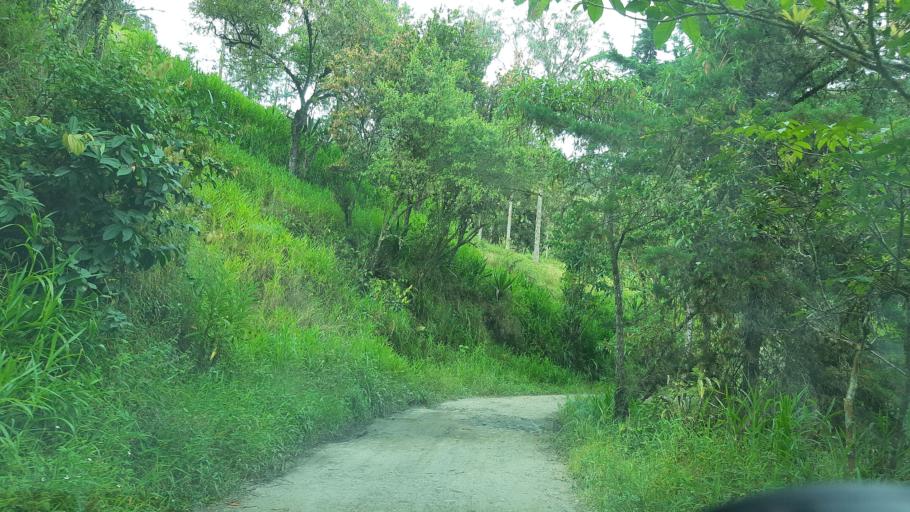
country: CO
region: Boyaca
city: Garagoa
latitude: 5.0411
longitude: -73.3400
